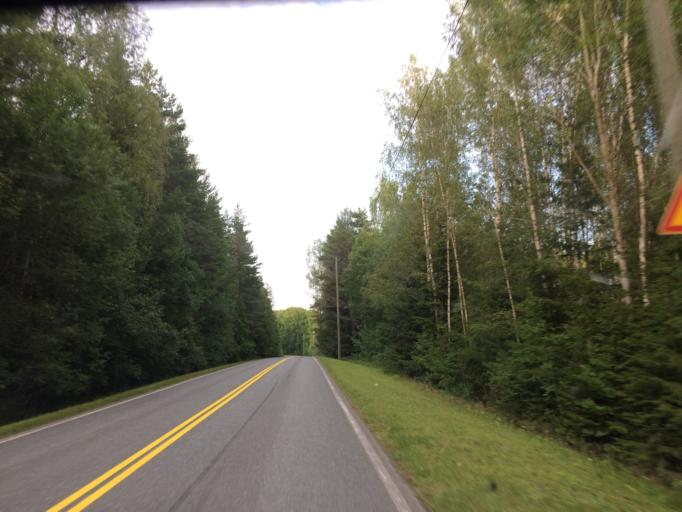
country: FI
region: Haeme
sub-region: Haemeenlinna
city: Janakkala
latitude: 60.8824
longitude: 24.5812
